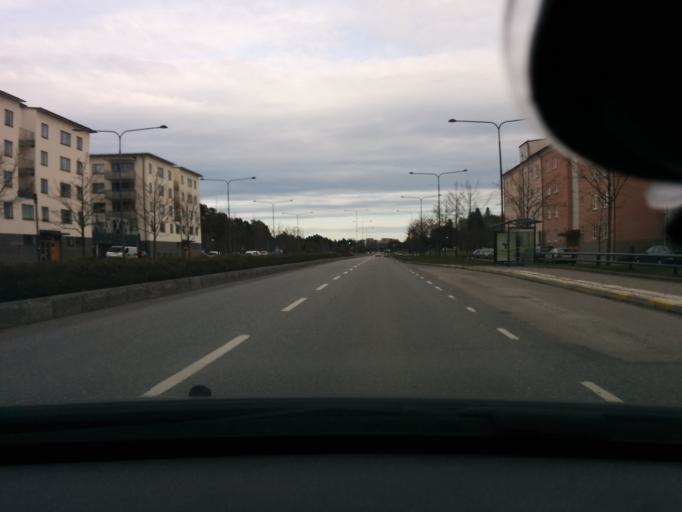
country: SE
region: Stockholm
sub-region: Jarfalla Kommun
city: Jakobsberg
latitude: 59.3718
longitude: 17.8456
